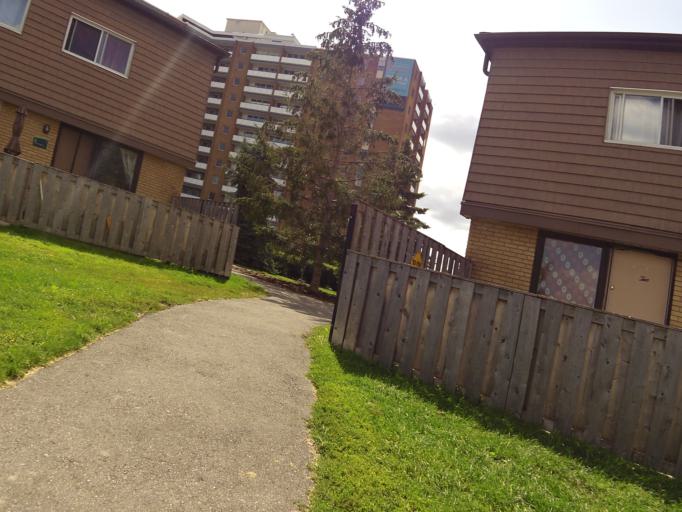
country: CA
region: Ontario
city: Bells Corners
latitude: 45.3469
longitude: -75.8122
